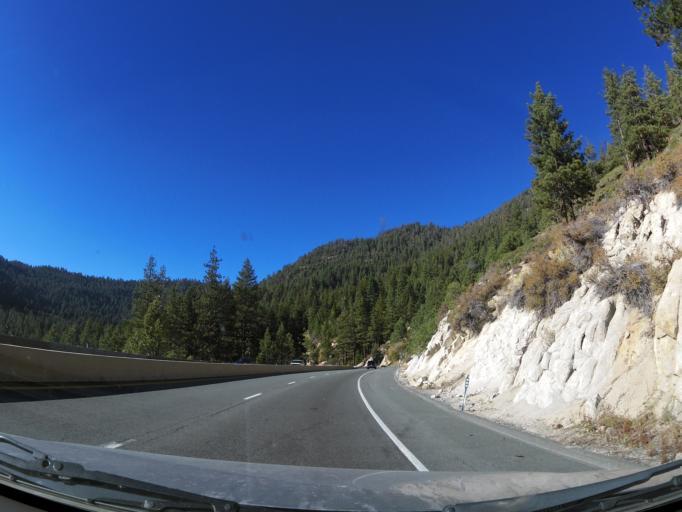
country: US
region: Nevada
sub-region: Douglas County
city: Indian Hills
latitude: 39.1171
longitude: -119.8714
